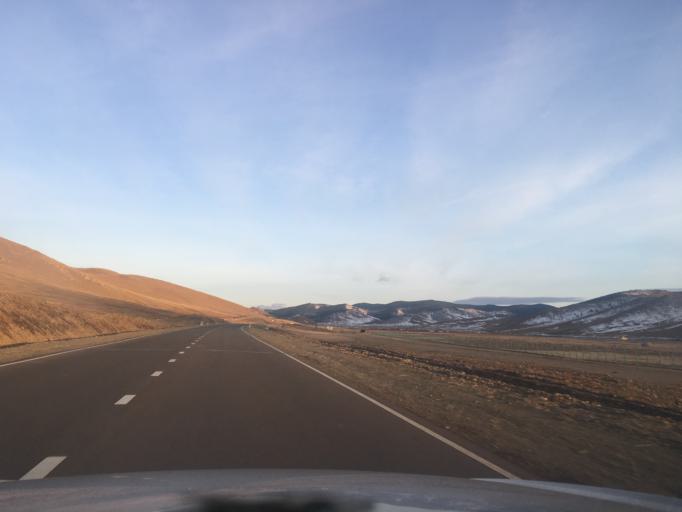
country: MN
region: Central Aimak
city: Mandal
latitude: 48.1145
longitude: 106.7007
